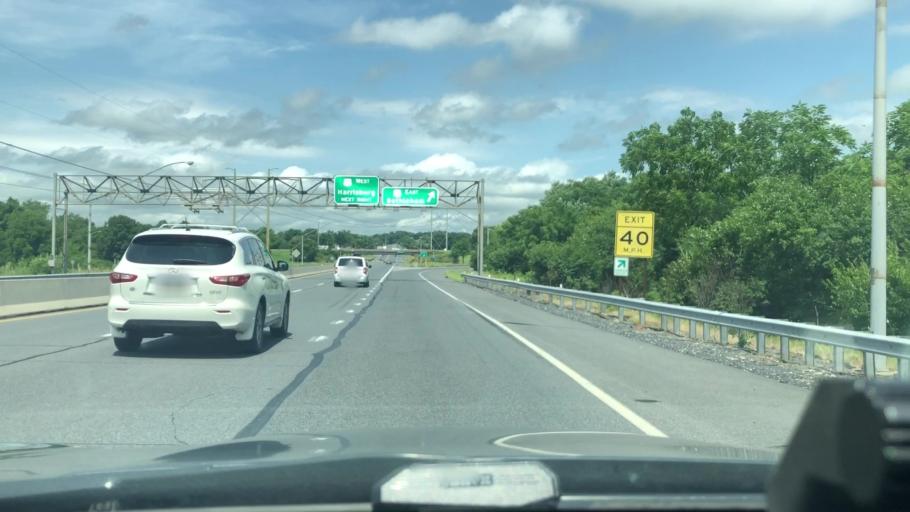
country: US
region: Pennsylvania
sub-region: Lehigh County
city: Wescosville
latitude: 40.5961
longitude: -75.5567
